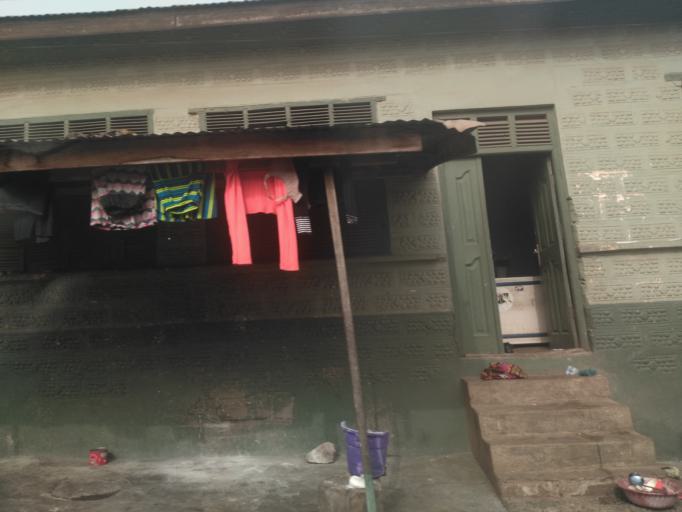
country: GH
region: Ashanti
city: Kumasi
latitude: 6.7044
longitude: -1.6214
